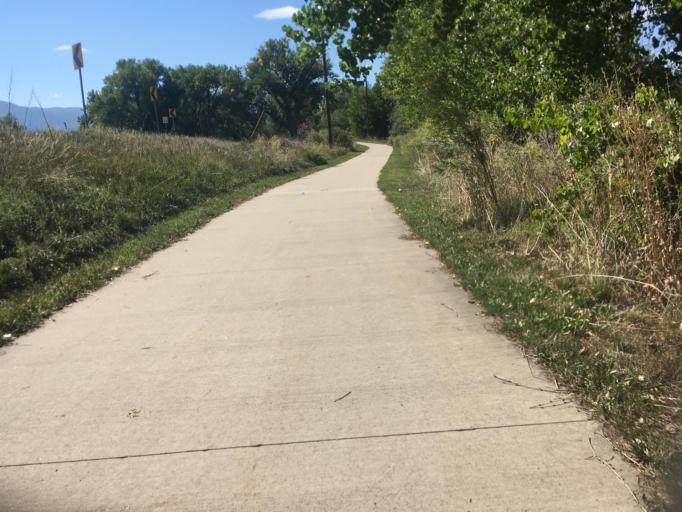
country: US
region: Colorado
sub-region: Boulder County
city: Boulder
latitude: 40.0294
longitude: -105.2217
